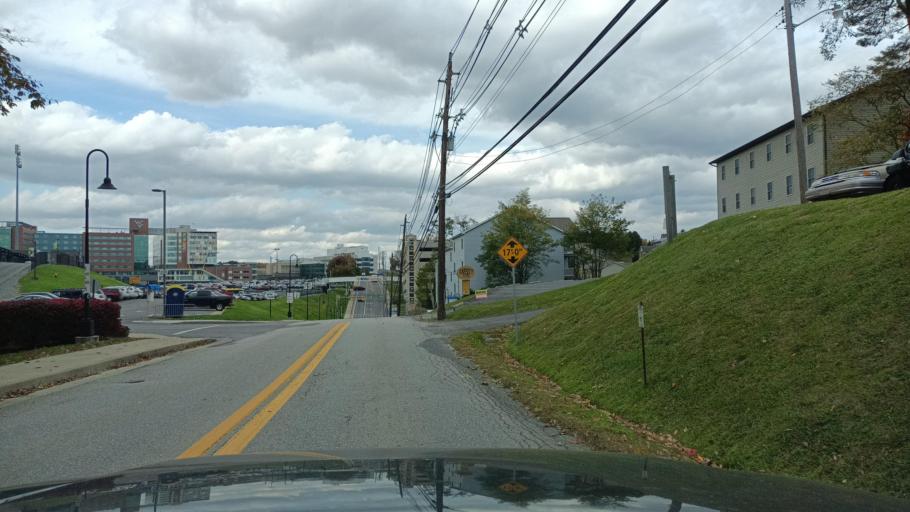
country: US
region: West Virginia
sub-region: Monongalia County
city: Morgantown
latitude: 39.6493
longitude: -79.9526
